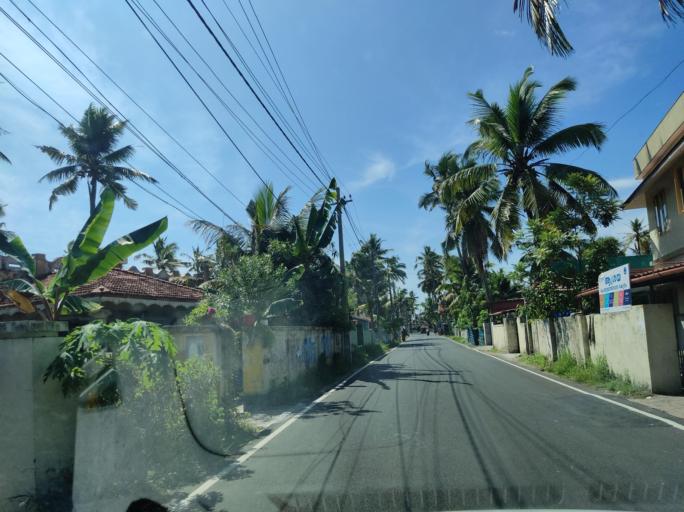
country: IN
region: Kerala
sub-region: Alappuzha
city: Kayankulam
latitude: 9.2452
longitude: 76.4136
